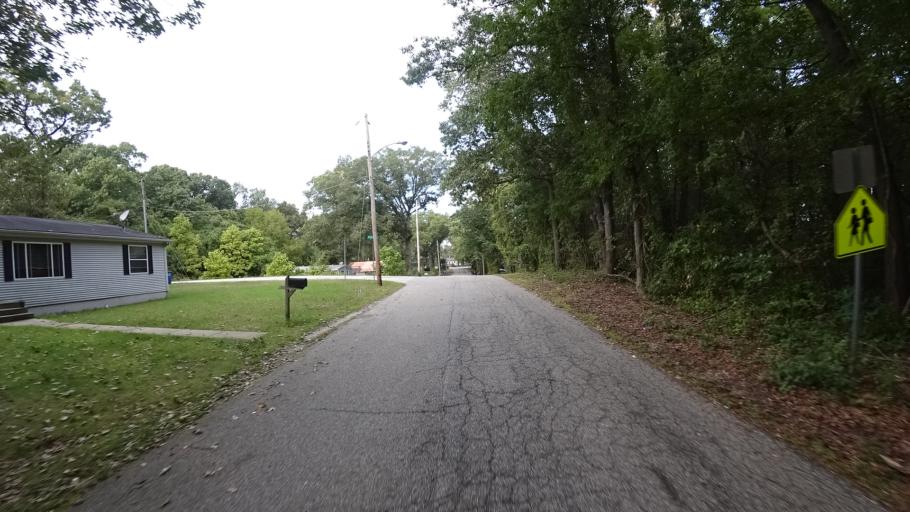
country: US
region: Indiana
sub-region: LaPorte County
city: Long Beach
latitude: 41.7292
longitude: -86.8612
